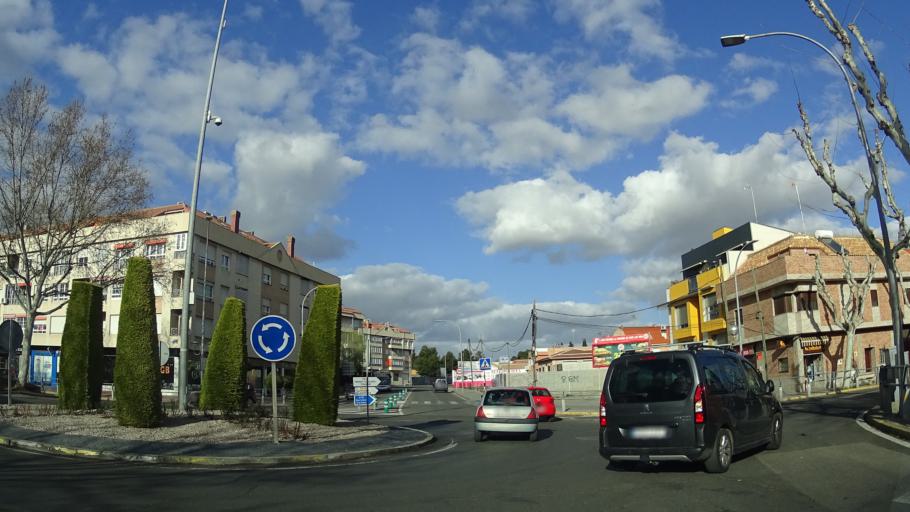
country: ES
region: Castille-La Mancha
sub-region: Provincia de Ciudad Real
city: Ciudad Real
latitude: 38.9816
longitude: -3.9252
